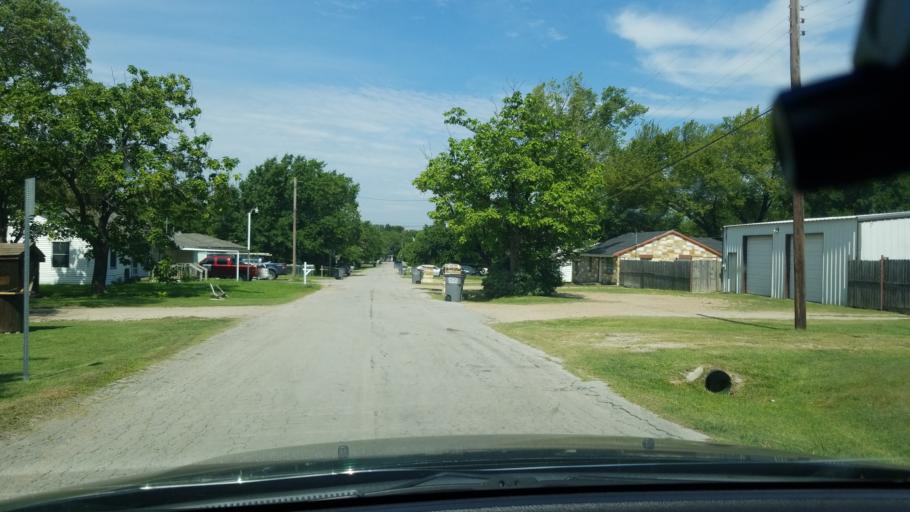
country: US
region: Texas
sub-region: Dallas County
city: Balch Springs
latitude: 32.7261
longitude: -96.6237
